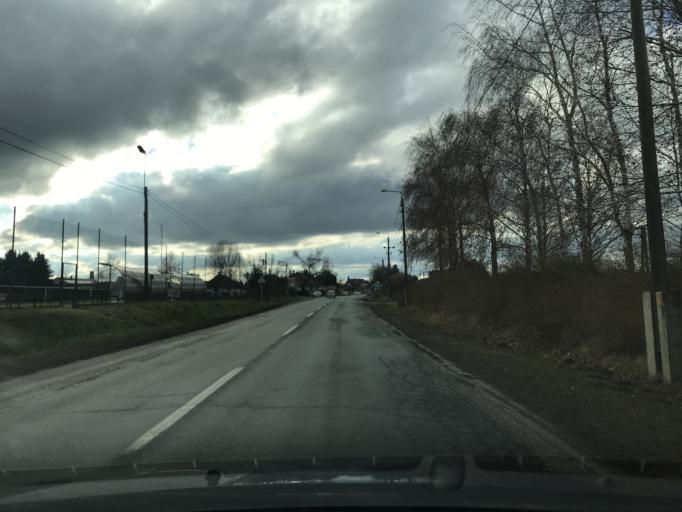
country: HU
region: Bacs-Kiskun
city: Nemesnadudvar
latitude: 46.3340
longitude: 19.0604
